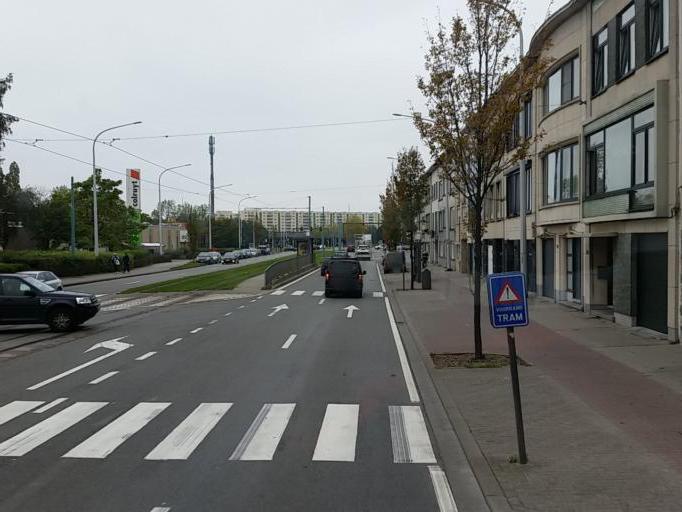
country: BE
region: Flanders
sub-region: Provincie Antwerpen
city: Antwerpen
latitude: 51.2427
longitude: 4.4317
